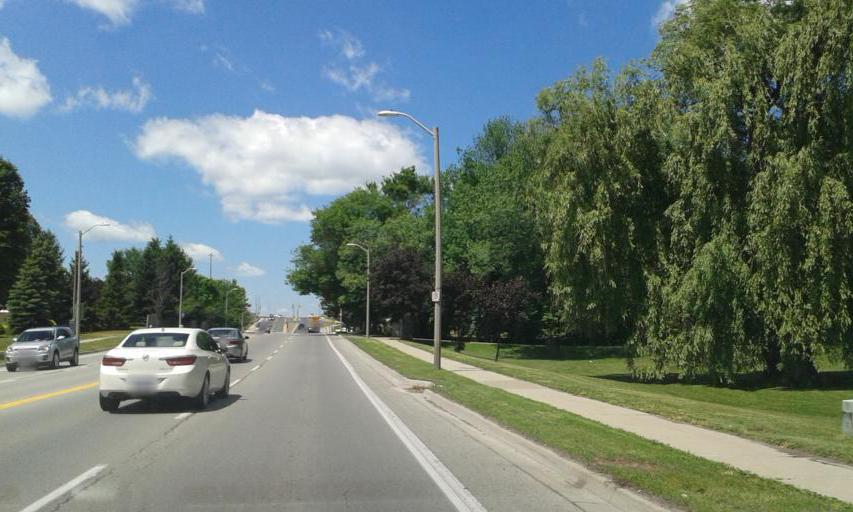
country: CA
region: Ontario
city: Niagara Falls
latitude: 43.1150
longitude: -79.1139
